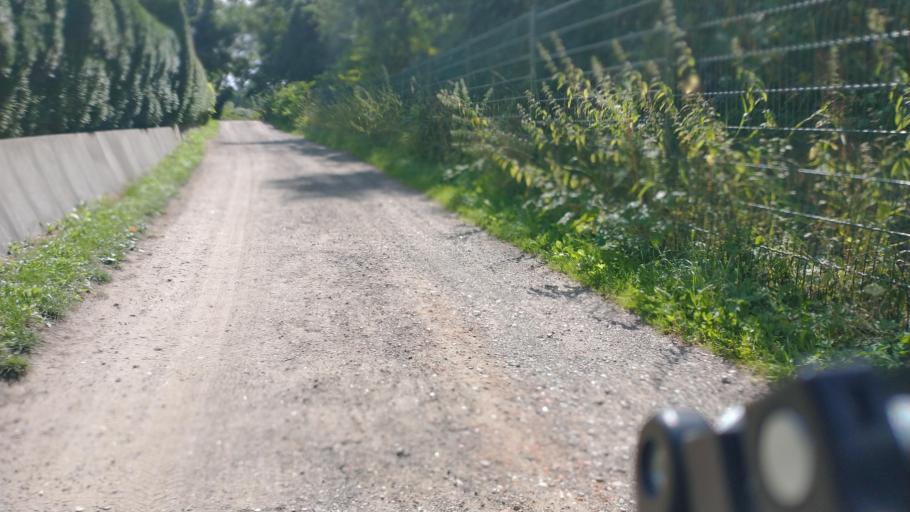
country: DE
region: Schleswig-Holstein
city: Bad Oldesloe
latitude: 53.8134
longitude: 10.3550
